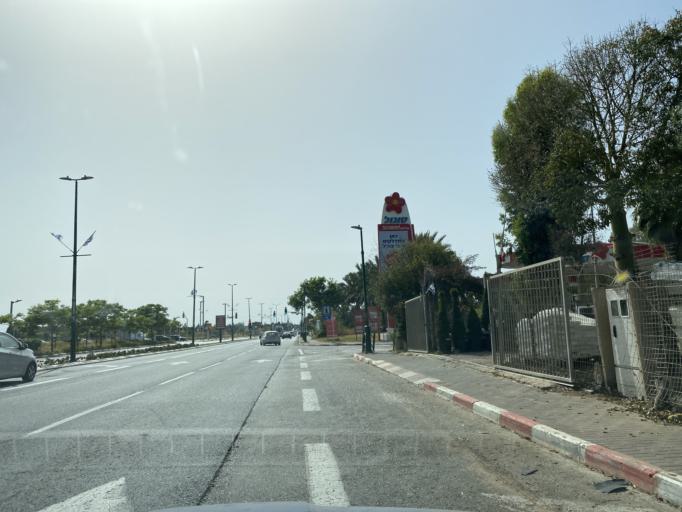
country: IL
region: Tel Aviv
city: Kefar Shemaryahu
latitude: 32.1783
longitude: 34.8317
